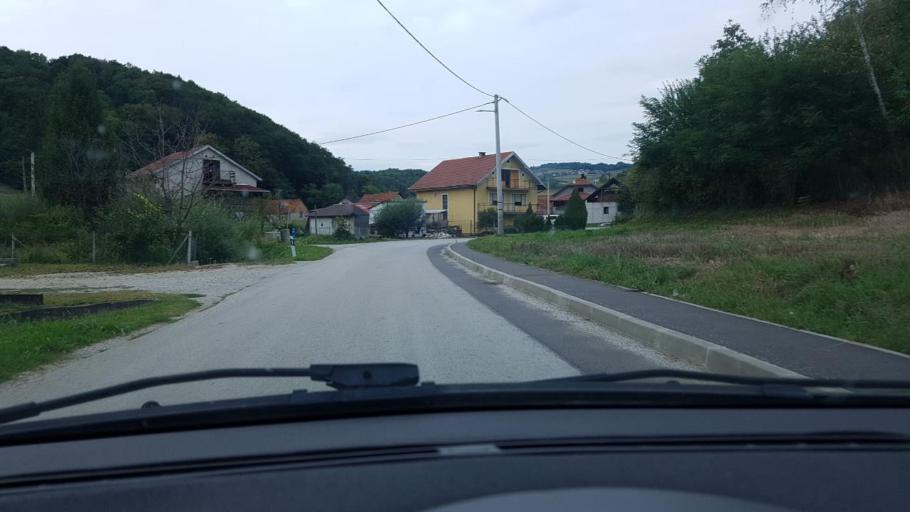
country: HR
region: Krapinsko-Zagorska
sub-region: Grad Krapina
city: Krapina
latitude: 46.1551
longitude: 15.8379
